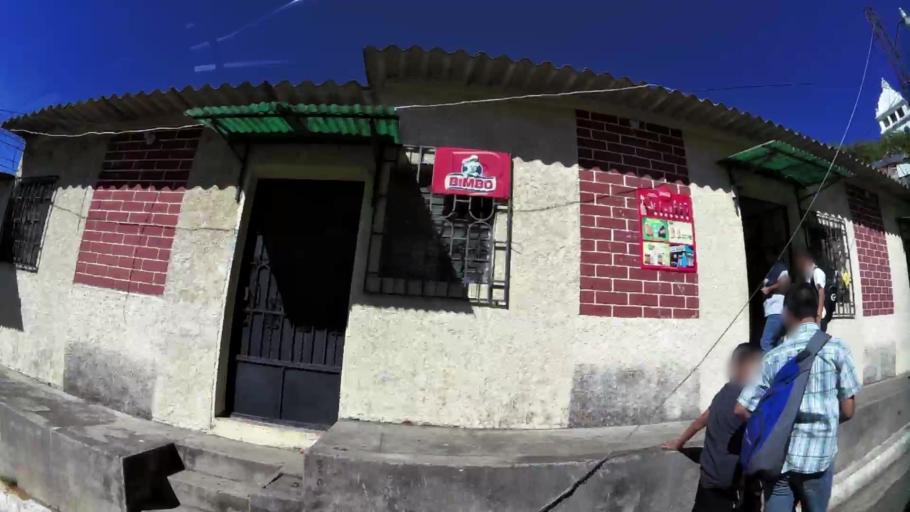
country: SV
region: Sonsonate
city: Juayua
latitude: 13.8424
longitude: -89.7473
